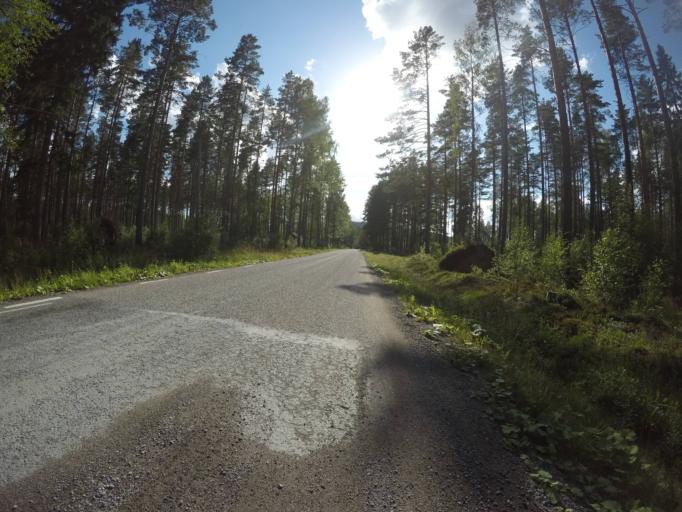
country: SE
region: OErebro
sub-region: Hallefors Kommun
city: Haellefors
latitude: 59.9064
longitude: 14.5538
